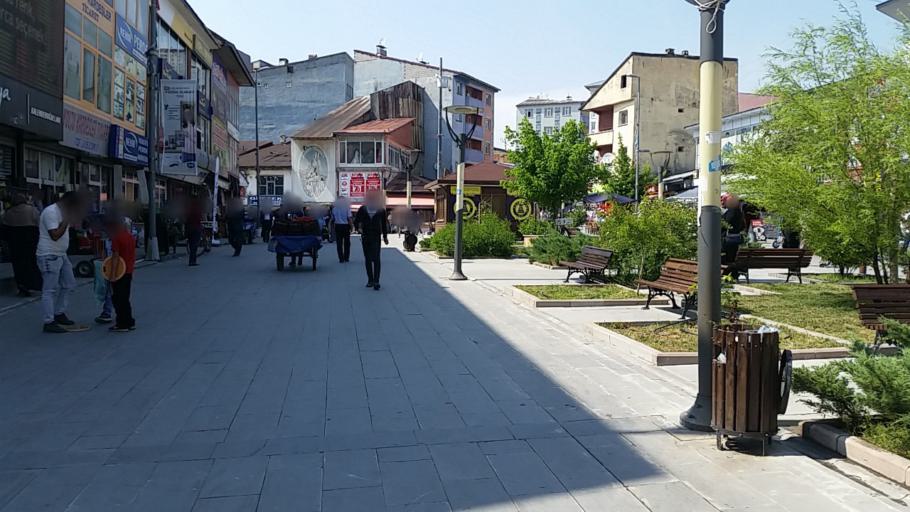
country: TR
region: Agri
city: Agri
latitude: 39.7173
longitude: 43.0515
